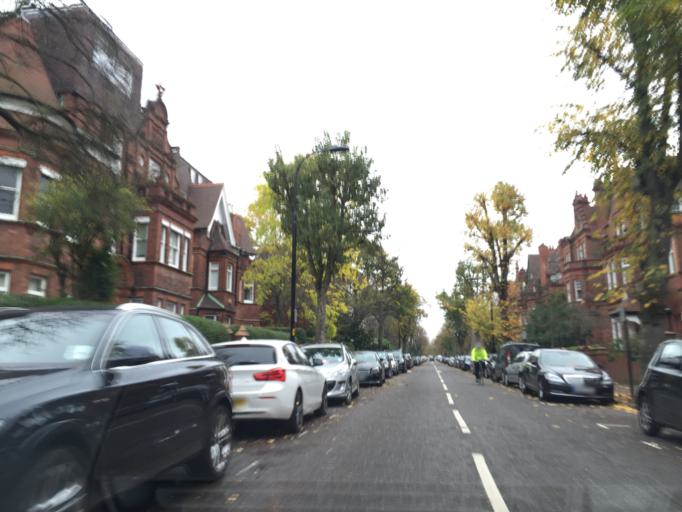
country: GB
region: England
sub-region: Greater London
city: Belsize Park
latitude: 51.5443
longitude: -0.1722
